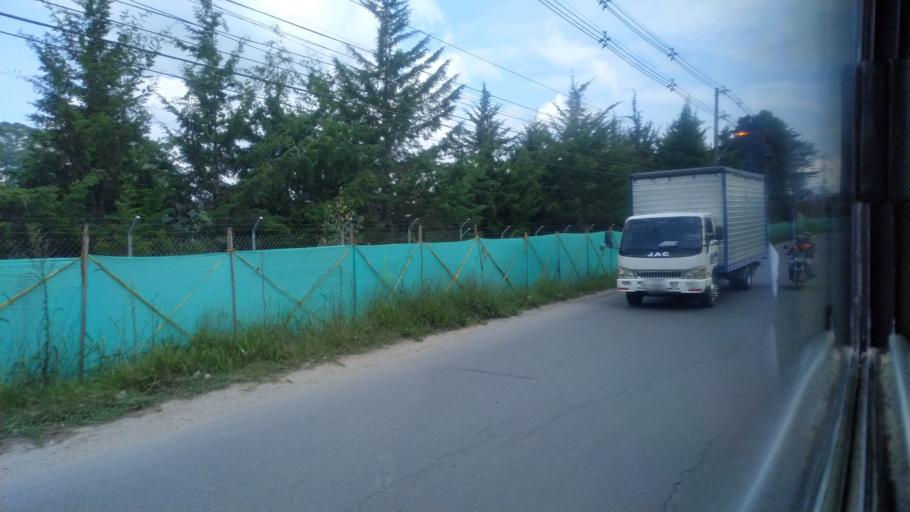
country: CO
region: Antioquia
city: Rionegro
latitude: 6.1695
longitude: -75.3689
